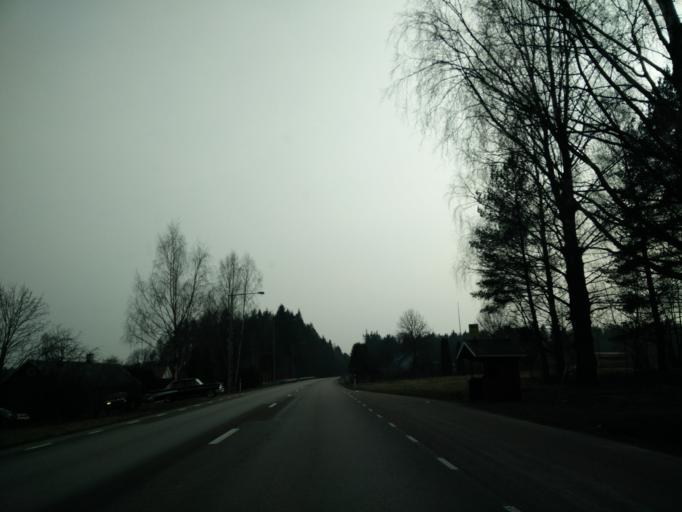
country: SE
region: Vaermland
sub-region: Forshaga Kommun
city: Forshaga
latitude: 59.4925
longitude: 13.4258
